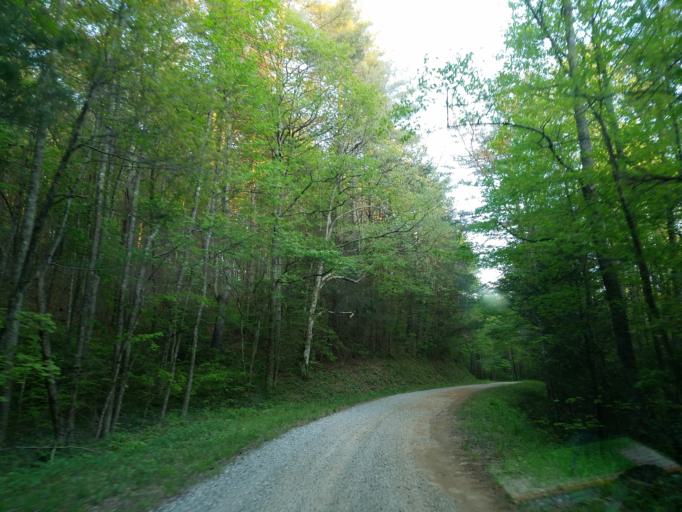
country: US
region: Georgia
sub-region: Union County
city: Blairsville
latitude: 34.7509
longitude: -83.9955
